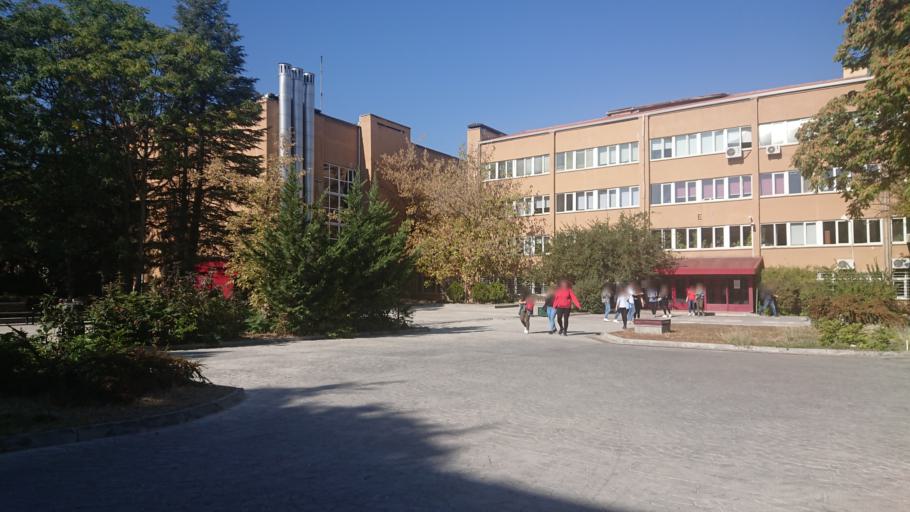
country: TR
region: Ankara
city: Ankara
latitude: 39.9351
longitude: 32.8307
